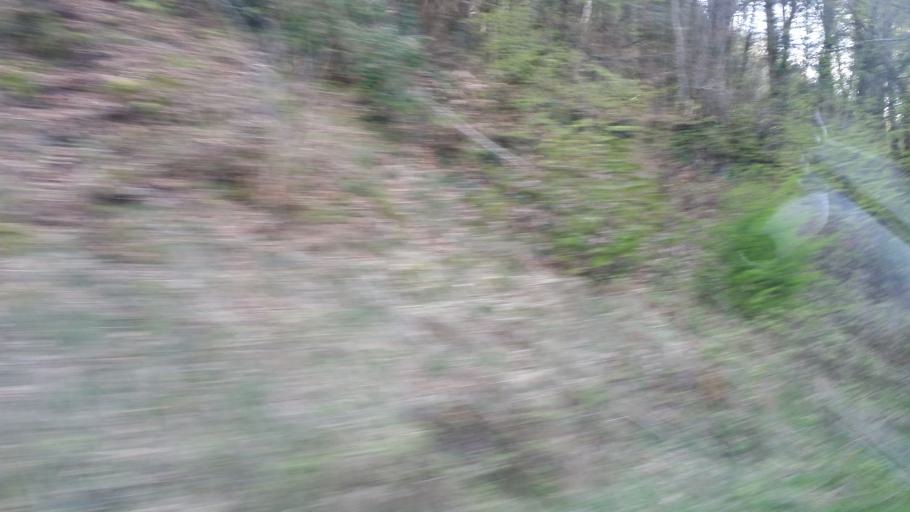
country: GB
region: Northern Ireland
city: Irvinestown
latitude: 54.4188
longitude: -7.7342
